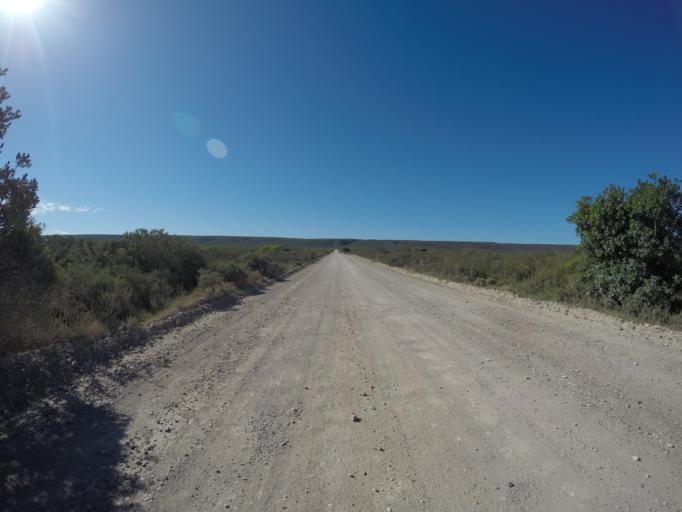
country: ZA
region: Western Cape
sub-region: Overberg District Municipality
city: Bredasdorp
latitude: -34.4437
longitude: 20.4216
